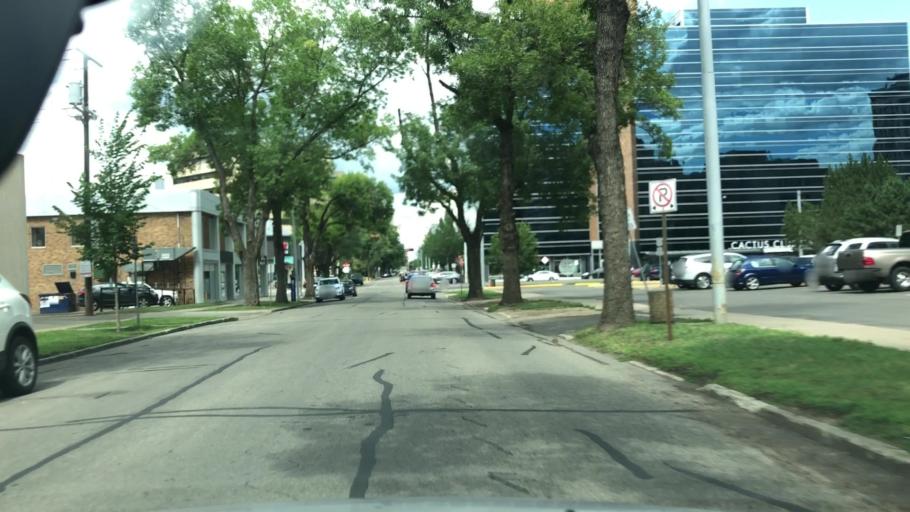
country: CA
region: Alberta
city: Edmonton
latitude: 53.5400
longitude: -113.5140
